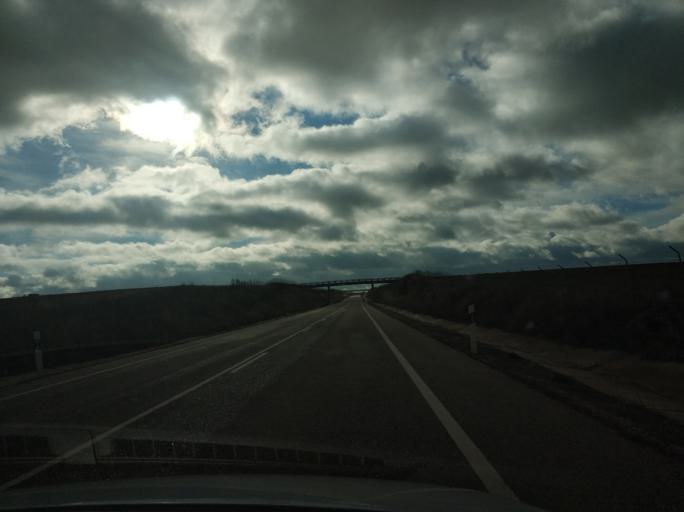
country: ES
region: Castille and Leon
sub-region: Provincia de Segovia
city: Ayllon
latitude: 41.4261
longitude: -3.3899
